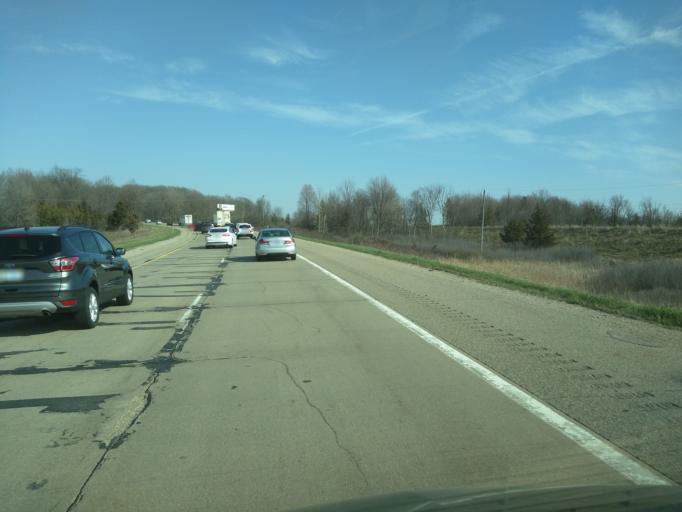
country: US
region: Michigan
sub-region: Kent County
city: Forest Hills
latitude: 42.8909
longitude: -85.5043
